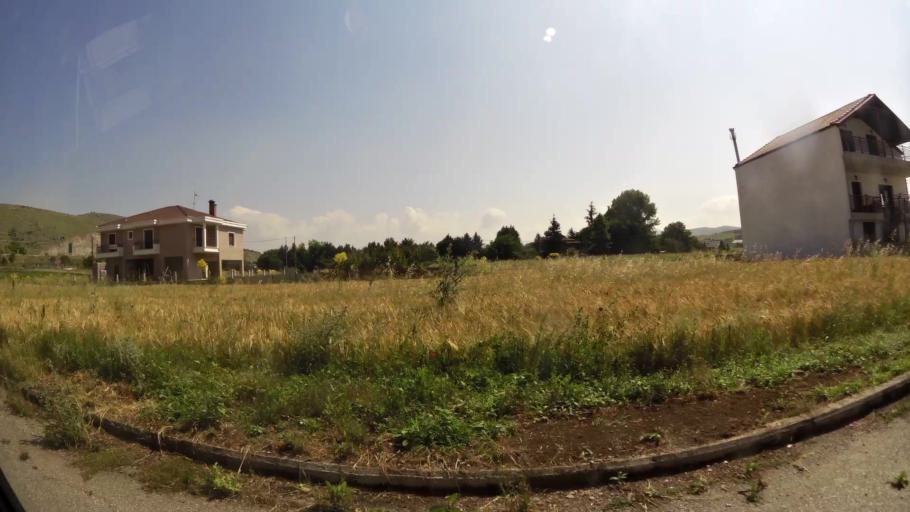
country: GR
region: West Macedonia
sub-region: Nomos Kozanis
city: Koila
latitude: 40.3402
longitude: 21.7885
